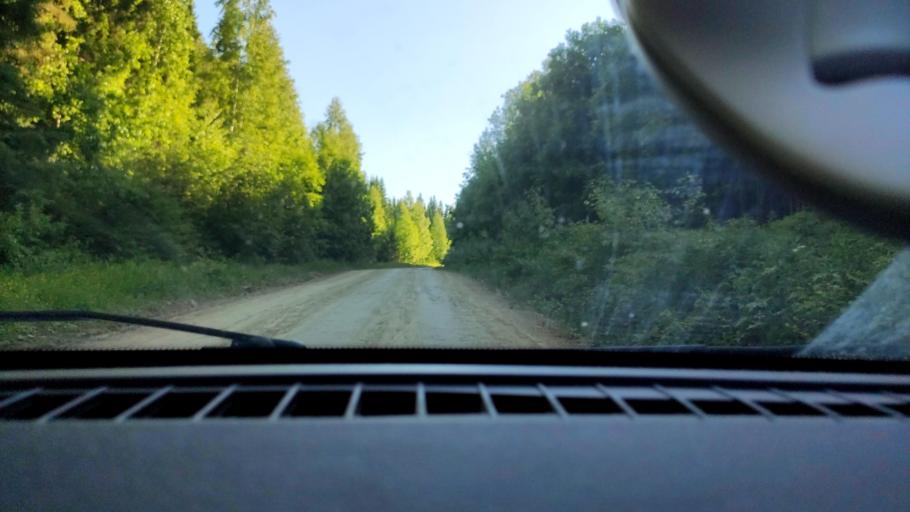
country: RU
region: Perm
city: Novyye Lyady
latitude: 58.1821
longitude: 56.5728
